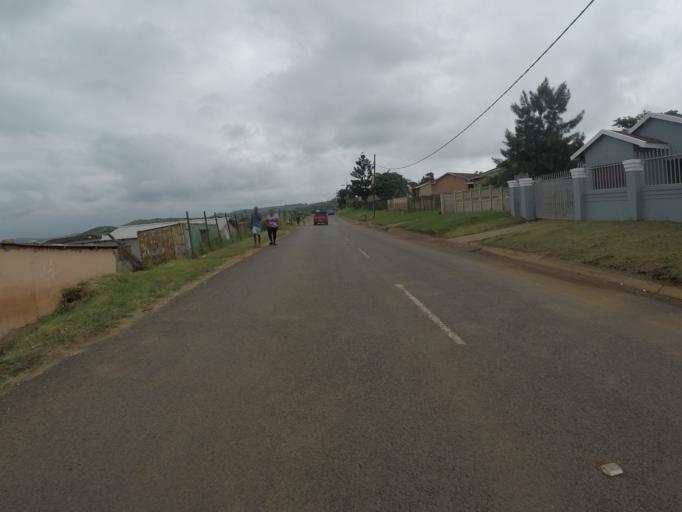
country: ZA
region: KwaZulu-Natal
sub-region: uThungulu District Municipality
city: Empangeni
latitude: -28.7785
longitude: 31.8492
